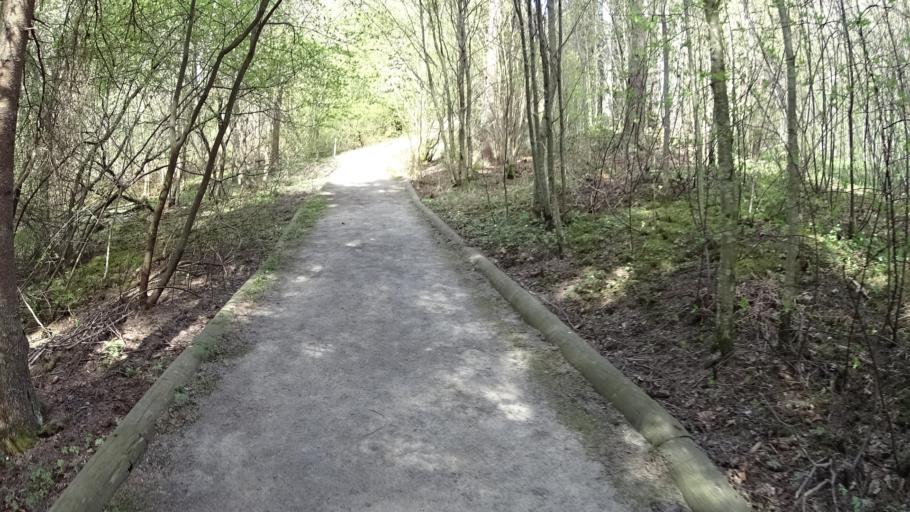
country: FI
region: Uusimaa
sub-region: Helsinki
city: Siuntio
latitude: 60.1669
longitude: 24.2136
